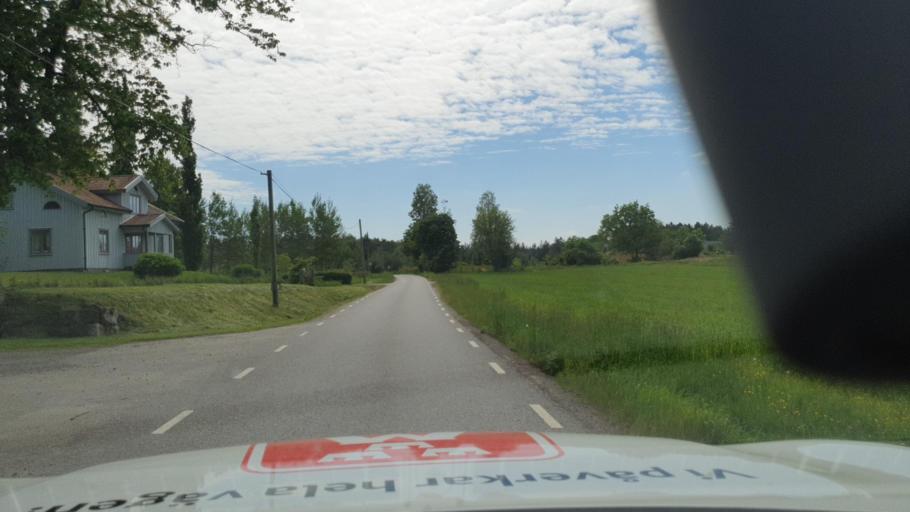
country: SE
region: Vaestra Goetaland
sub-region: Alingsas Kommun
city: Sollebrunn
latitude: 58.2490
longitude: 12.4917
